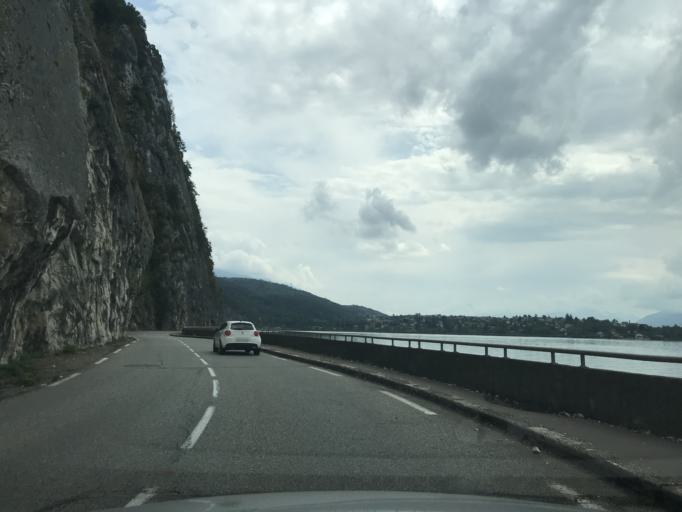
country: FR
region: Rhone-Alpes
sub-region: Departement de la Savoie
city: Brison-Saint-Innocent
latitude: 45.7471
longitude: 5.8842
